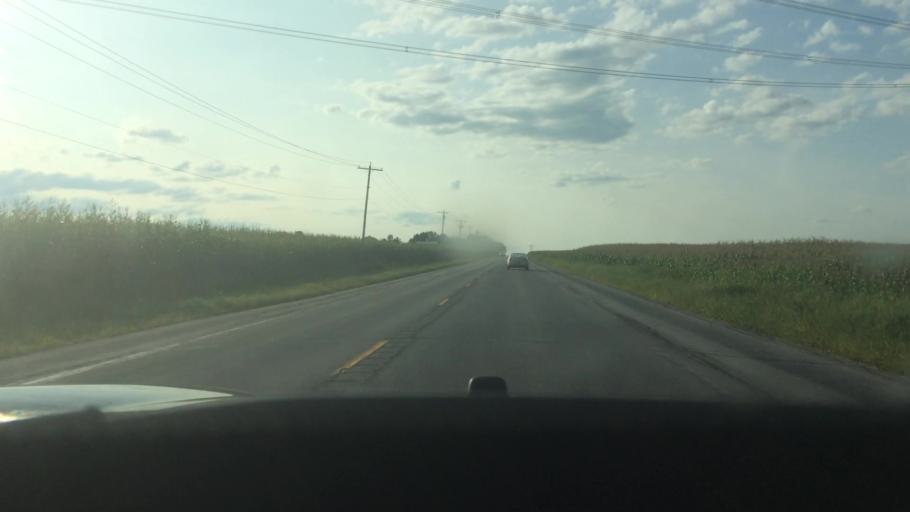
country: US
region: New York
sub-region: St. Lawrence County
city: Canton
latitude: 44.5988
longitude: -75.1934
